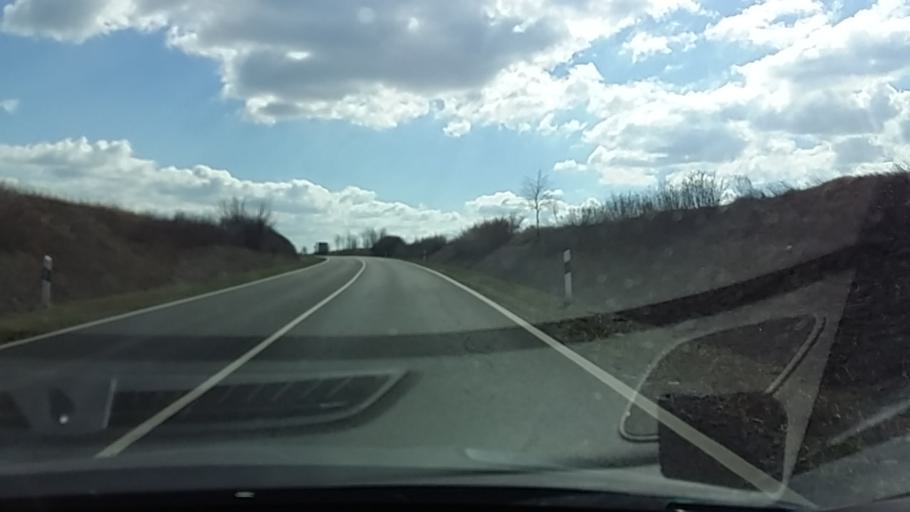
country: HU
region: Baranya
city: Kozarmisleny
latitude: 46.0434
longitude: 18.2718
